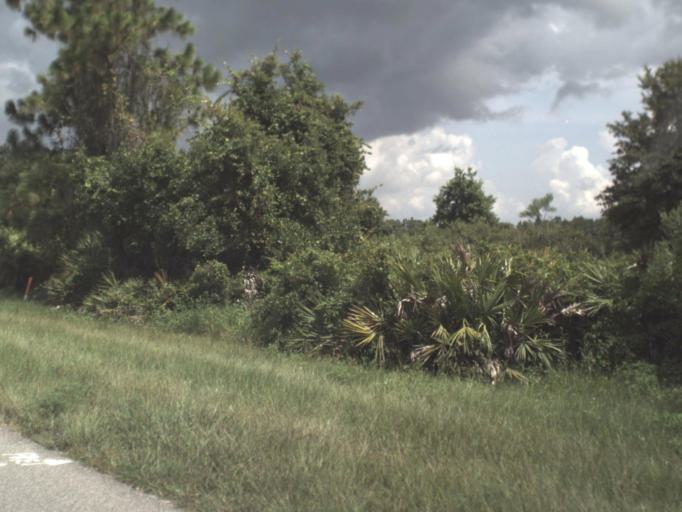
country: US
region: Florida
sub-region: Pasco County
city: Wesley Chapel
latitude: 28.2220
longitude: -82.2769
